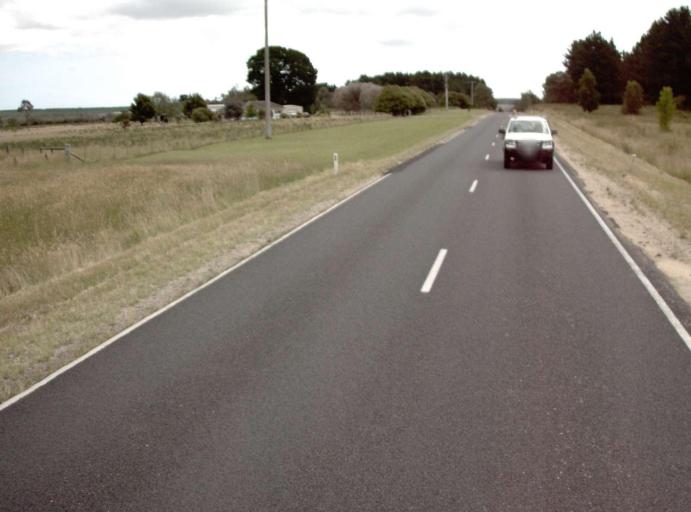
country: AU
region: Victoria
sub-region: Wellington
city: Sale
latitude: -38.1691
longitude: 147.0354
